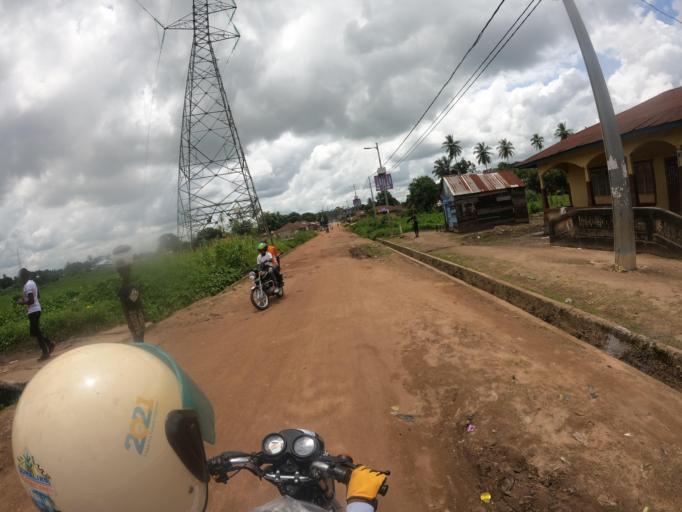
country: SL
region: Northern Province
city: Makeni
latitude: 8.8899
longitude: -12.0502
